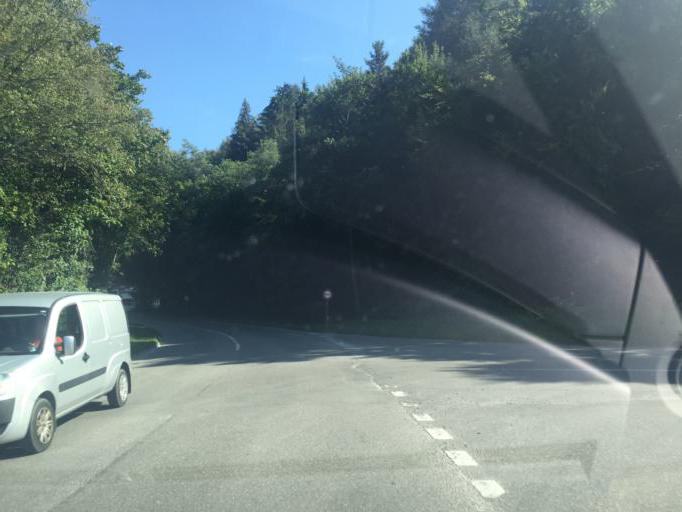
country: CH
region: Schaffhausen
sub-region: Bezirk Reiat
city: Stetten
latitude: 47.7138
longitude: 8.6650
